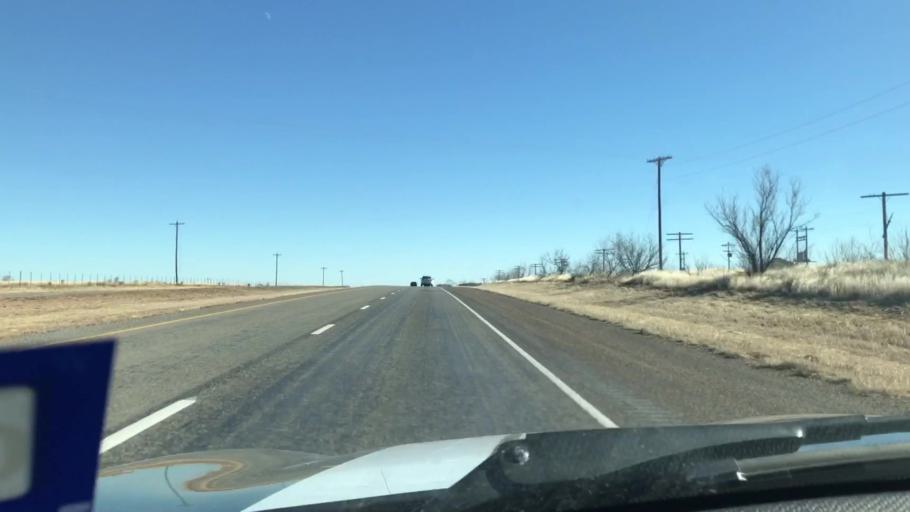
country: US
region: Texas
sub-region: Garza County
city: Post
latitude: 33.1350
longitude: -101.3077
